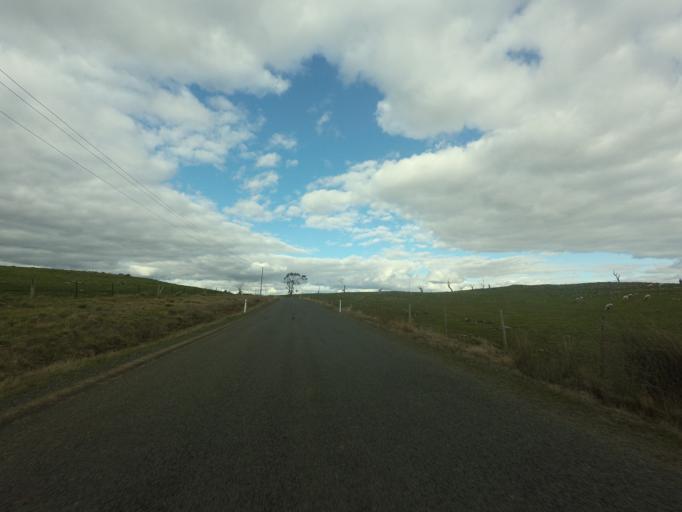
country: AU
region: Tasmania
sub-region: Northern Midlands
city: Evandale
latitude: -41.8953
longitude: 147.4248
